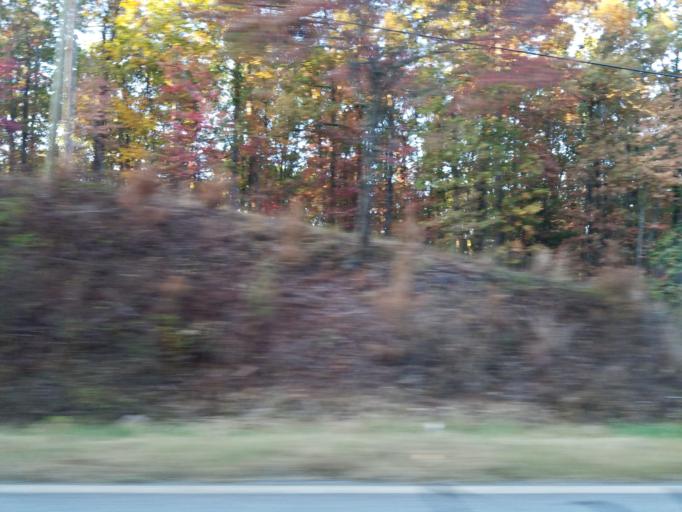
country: US
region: Georgia
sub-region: Lumpkin County
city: Dahlonega
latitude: 34.5492
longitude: -84.0998
